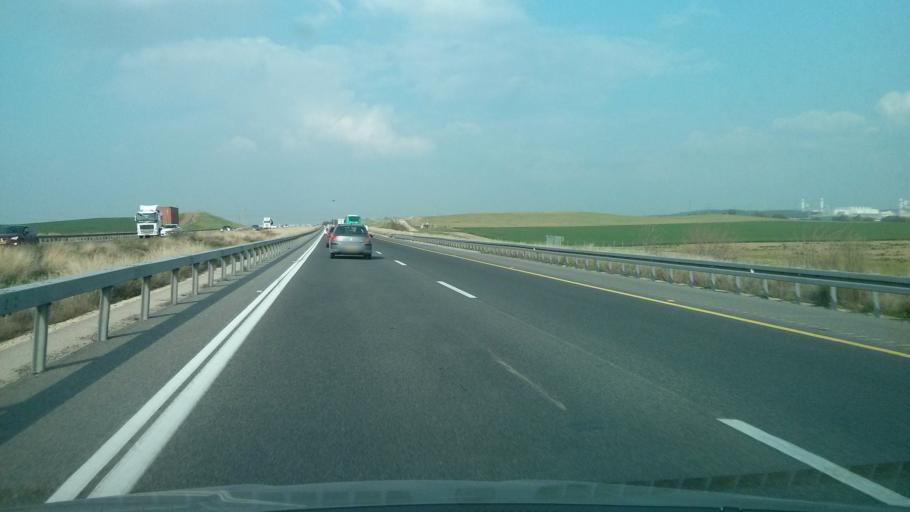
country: IL
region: Southern District
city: Qiryat Gat
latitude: 31.6993
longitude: 34.8166
